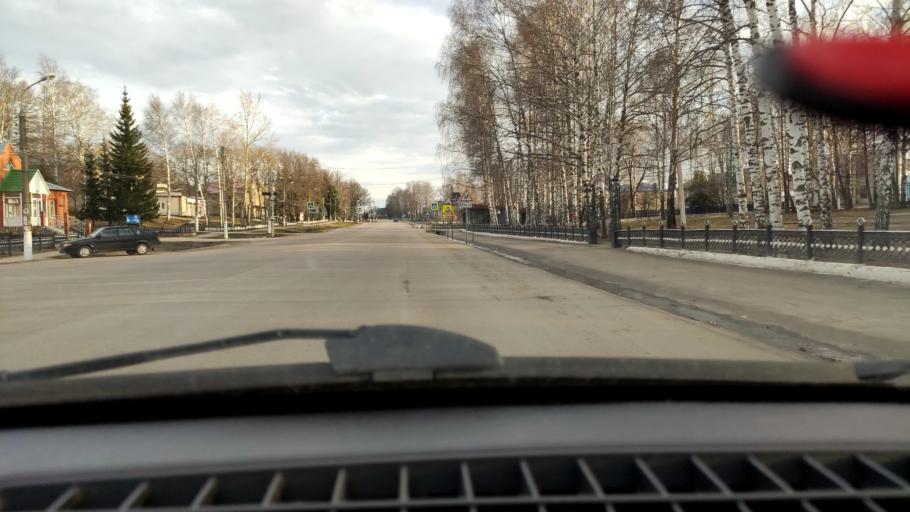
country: RU
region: Bashkortostan
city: Tolbazy
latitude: 54.0155
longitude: 55.8863
